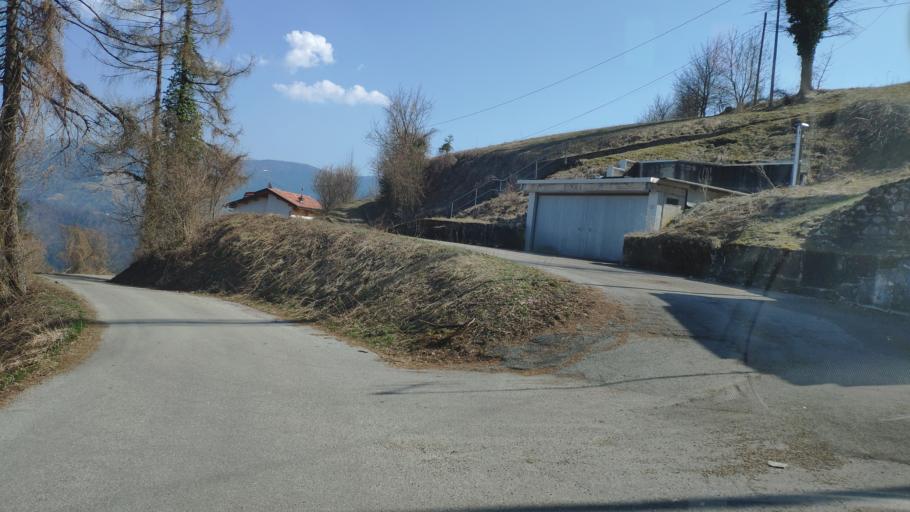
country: IT
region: Veneto
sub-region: Provincia di Vicenza
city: Enego
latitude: 45.9493
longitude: 11.7015
